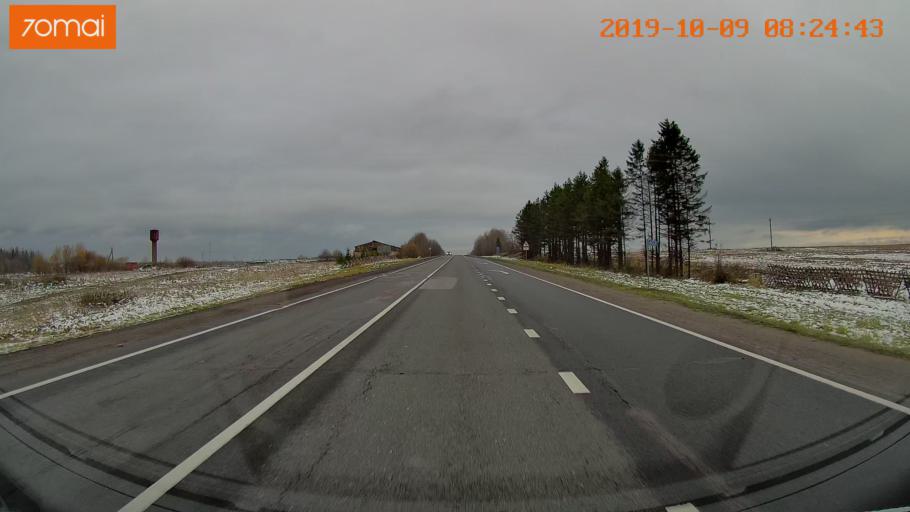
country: RU
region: Vologda
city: Gryazovets
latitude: 58.7703
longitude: 40.2767
